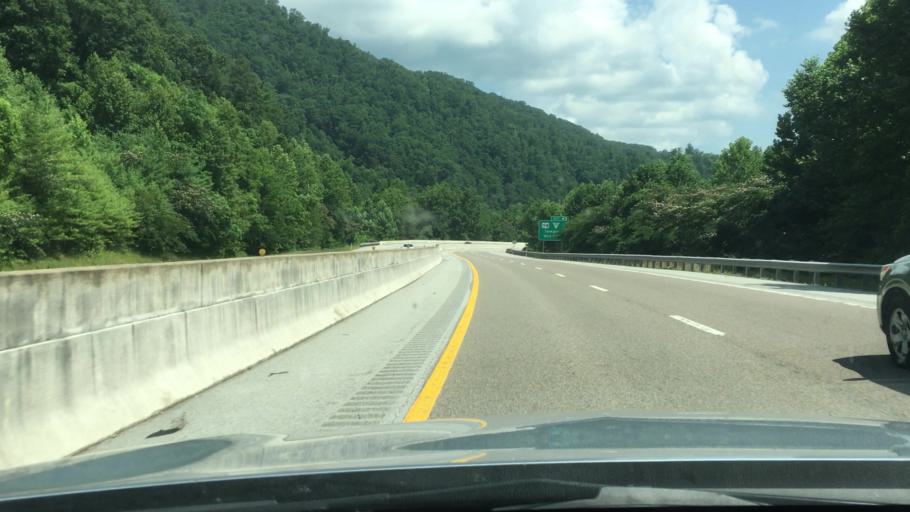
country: US
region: Tennessee
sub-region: Unicoi County
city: Banner Hill
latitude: 36.0819
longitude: -82.4948
